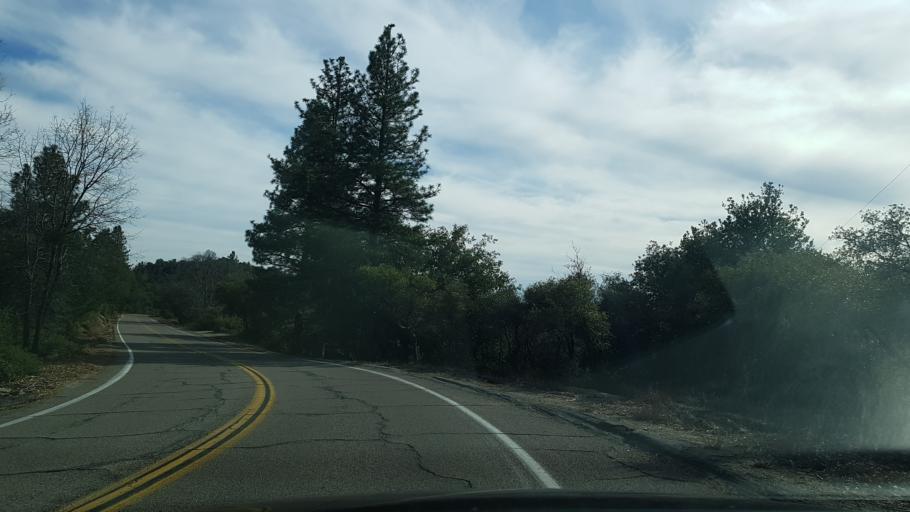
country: US
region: California
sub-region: Riverside County
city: Aguanga
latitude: 33.3591
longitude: -116.8724
